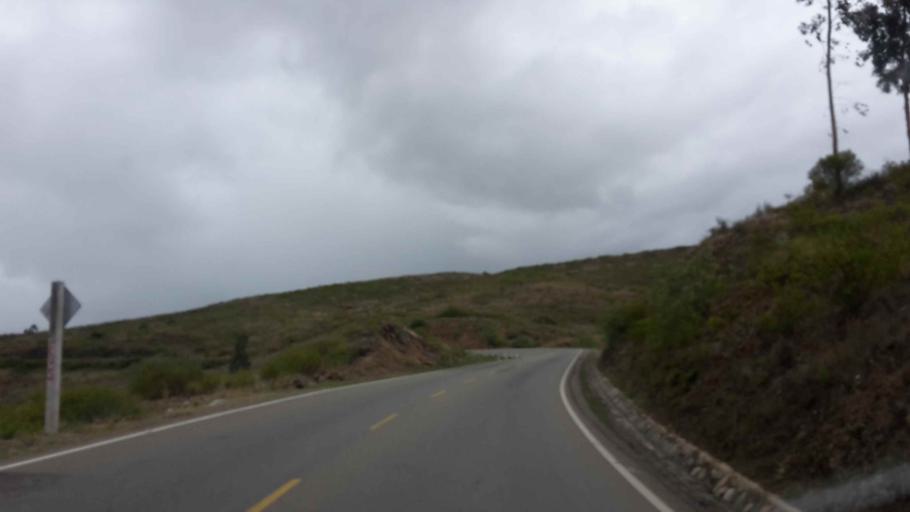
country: BO
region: Cochabamba
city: Arani
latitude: -17.4742
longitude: -65.7645
